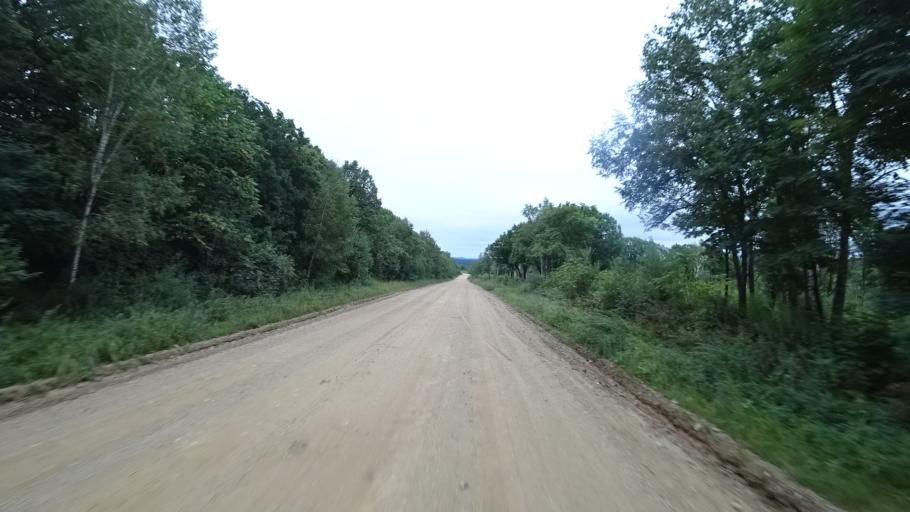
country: RU
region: Primorskiy
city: Rettikhovka
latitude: 44.1800
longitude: 132.8248
